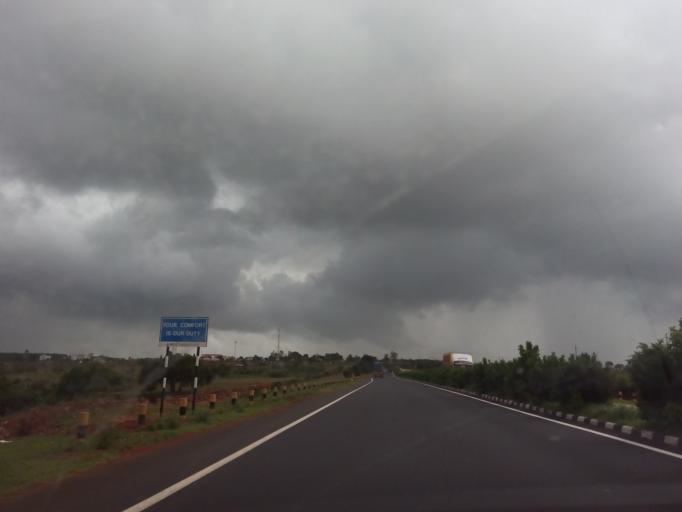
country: IN
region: Karnataka
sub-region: Belgaum
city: Belgaum
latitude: 16.0277
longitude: 74.5272
